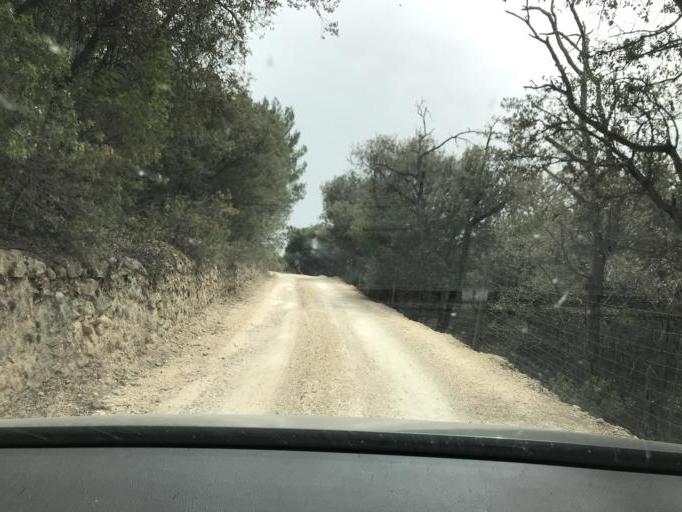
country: ES
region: Andalusia
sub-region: Provincia de Granada
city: Castril
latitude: 37.8368
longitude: -2.7735
